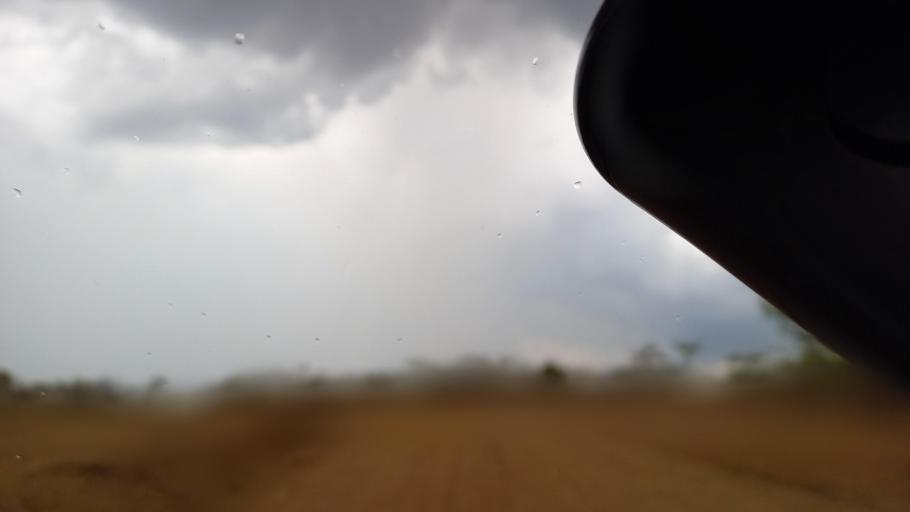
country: ZM
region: Lusaka
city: Kafue
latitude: -15.8681
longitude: 28.1898
